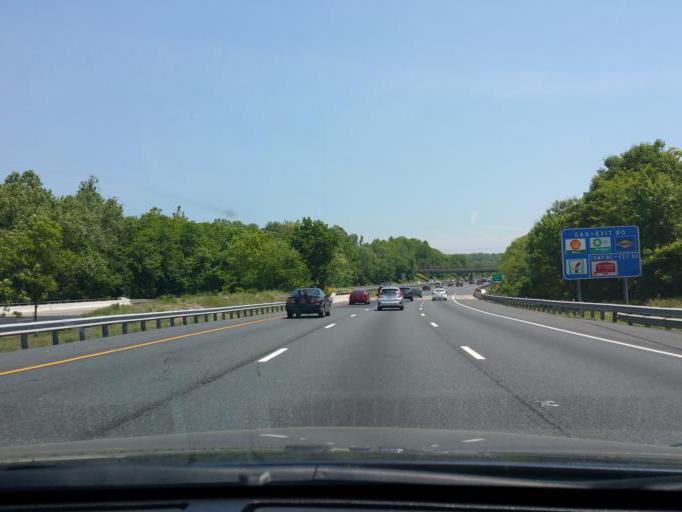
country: US
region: Maryland
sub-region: Harford County
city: Riverside
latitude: 39.4758
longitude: -76.2708
